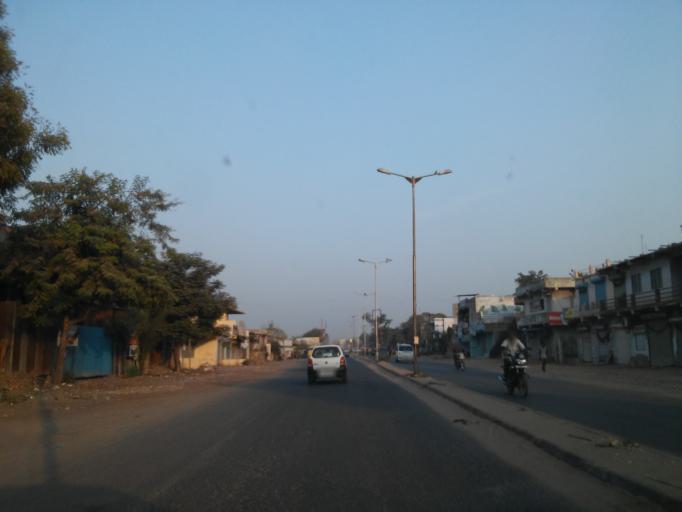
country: IN
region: Gujarat
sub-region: Ahmadabad
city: Sarkhej
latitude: 22.9872
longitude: 72.4958
